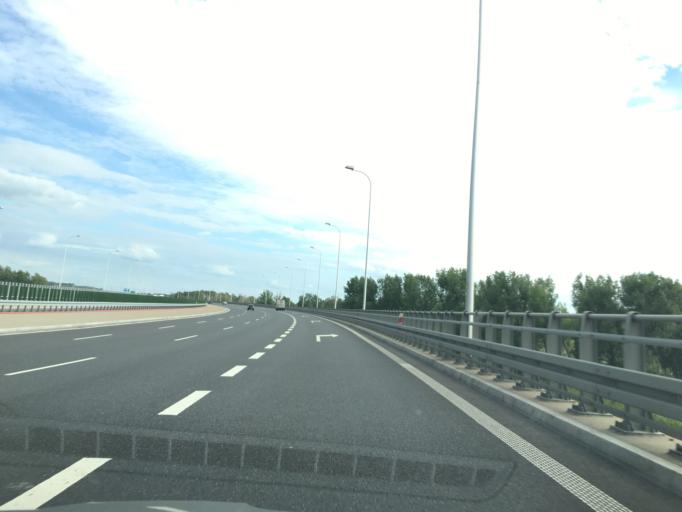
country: PL
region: Silesian Voivodeship
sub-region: Gliwice
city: Gliwice
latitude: 50.2874
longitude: 18.7149
